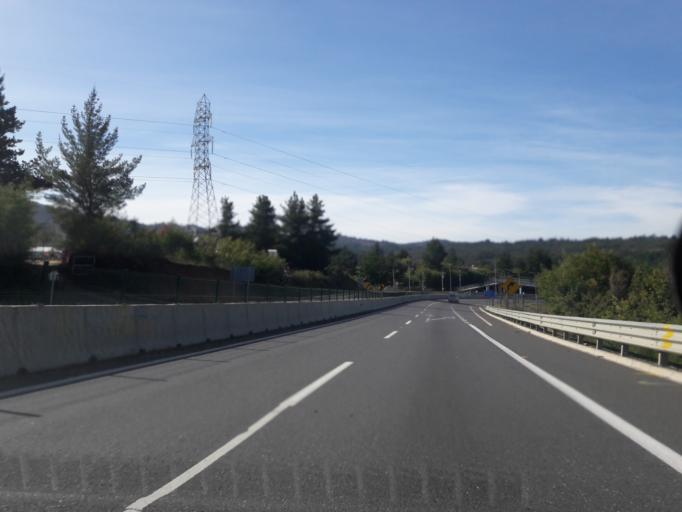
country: CL
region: Biobio
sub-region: Provincia de Biobio
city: Yumbel
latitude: -36.9772
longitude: -72.6414
